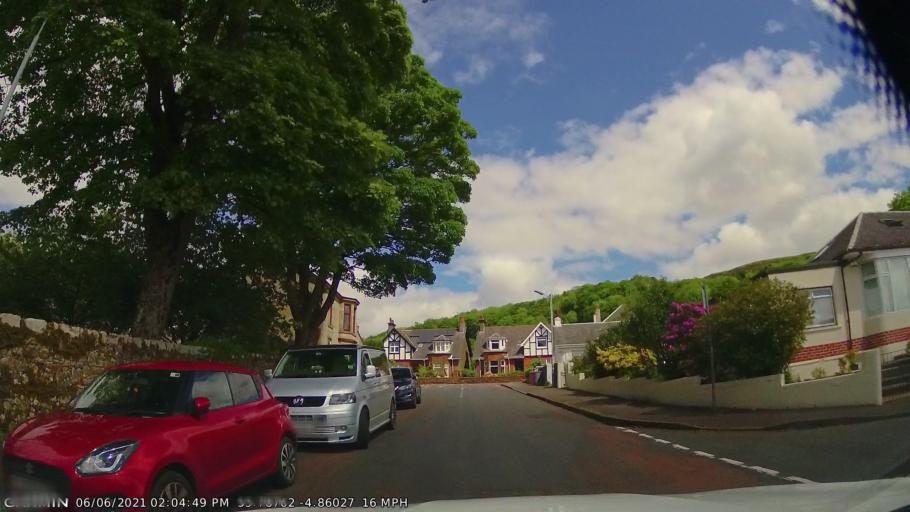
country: GB
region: Scotland
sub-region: North Ayrshire
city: Largs
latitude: 55.7876
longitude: -4.8602
